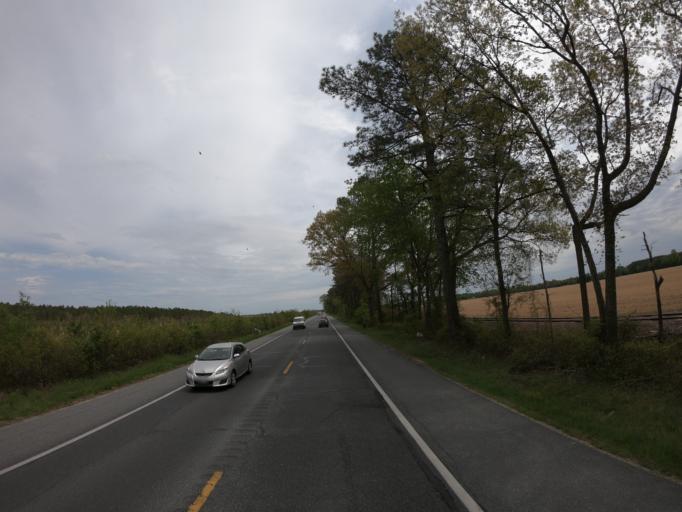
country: US
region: Delaware
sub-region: Sussex County
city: Milton
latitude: 38.7887
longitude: -75.3680
